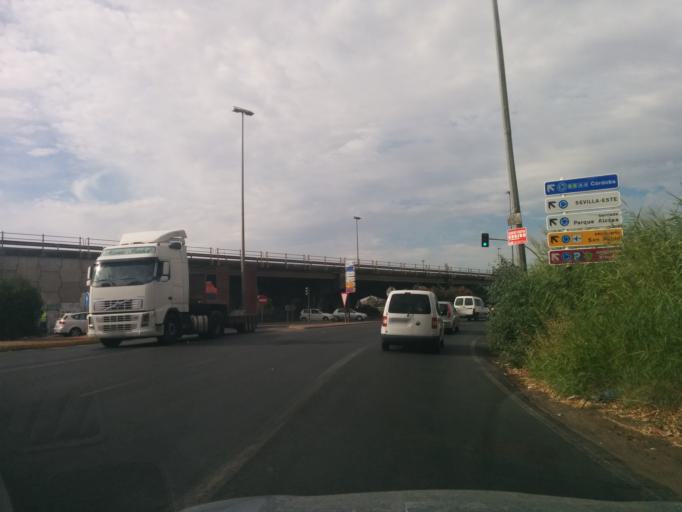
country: ES
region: Andalusia
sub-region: Provincia de Sevilla
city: Sevilla
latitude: 37.4148
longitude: -5.9305
